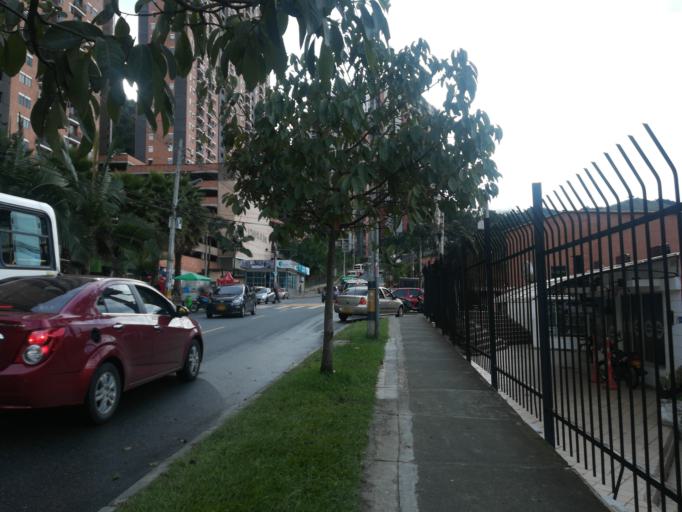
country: CO
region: Antioquia
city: Itagui
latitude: 6.2028
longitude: -75.6010
